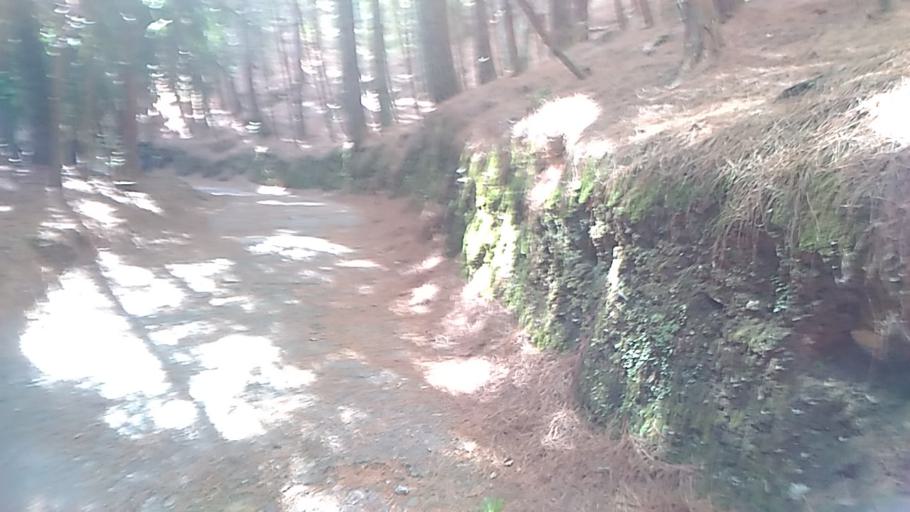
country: TW
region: Taiwan
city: Daxi
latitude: 24.4051
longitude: 121.3072
